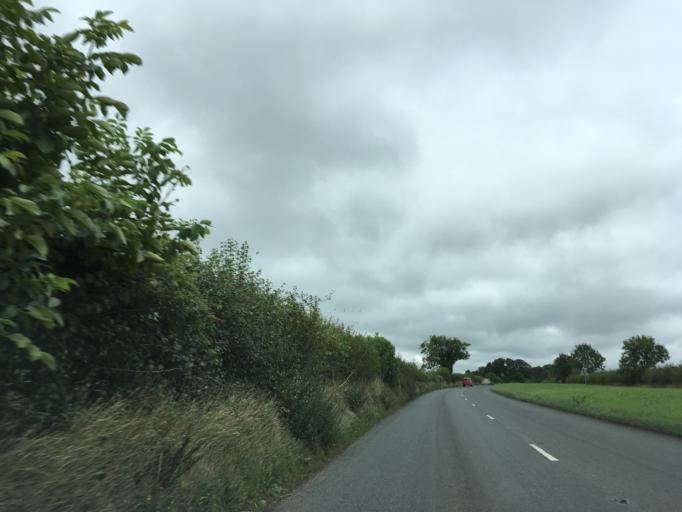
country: GB
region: England
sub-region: Bath and North East Somerset
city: Saltford
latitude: 51.3695
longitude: -2.4779
